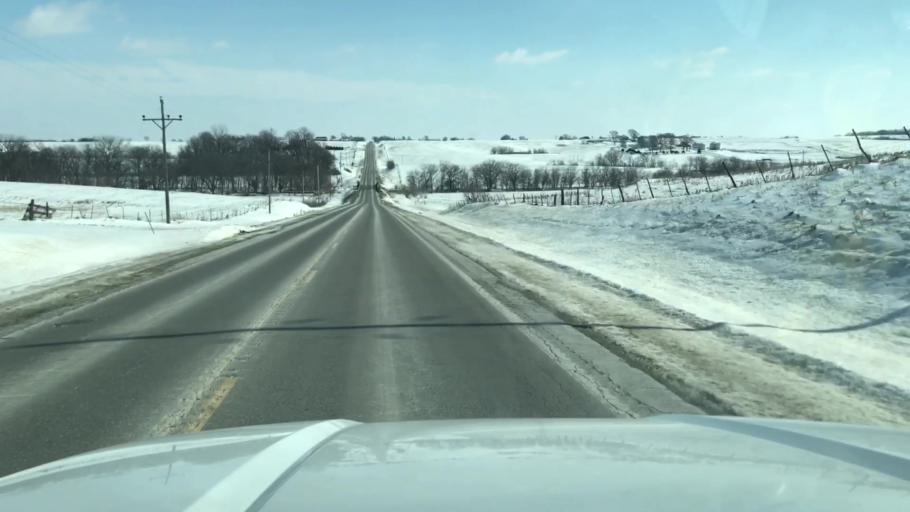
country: US
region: Missouri
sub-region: Nodaway County
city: Maryville
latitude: 40.3441
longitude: -94.7496
